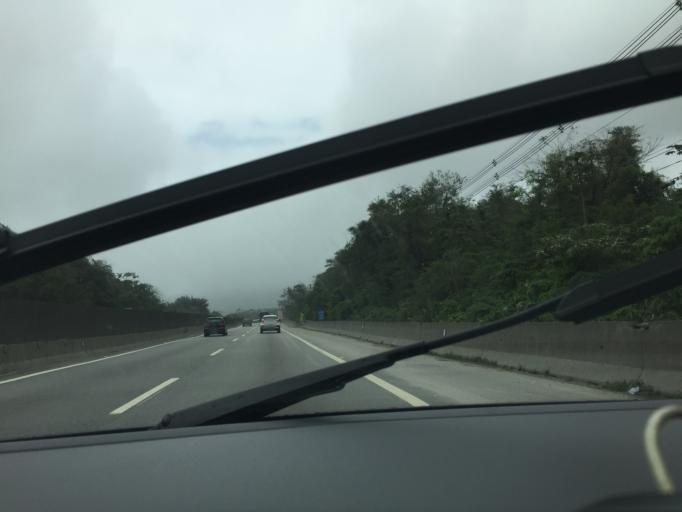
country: BR
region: Sao Paulo
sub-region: Santos
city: Santos
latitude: -23.8870
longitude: -46.3111
